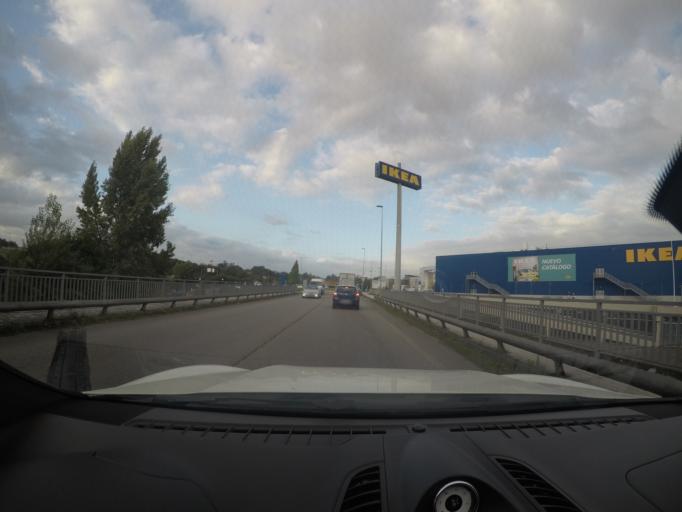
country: ES
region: Asturias
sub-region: Province of Asturias
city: Lugones
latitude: 43.3876
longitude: -5.8080
